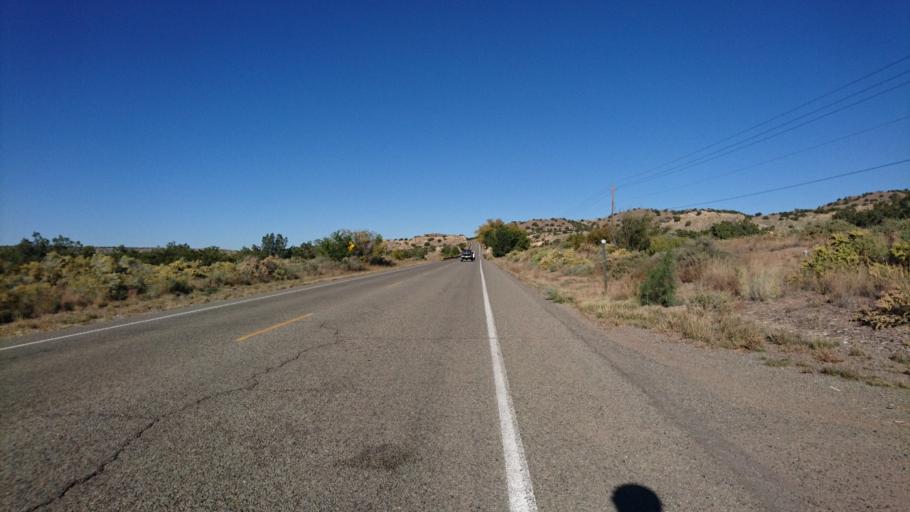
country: US
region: New Mexico
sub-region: Santa Fe County
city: La Cienega
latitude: 35.4317
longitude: -106.0995
